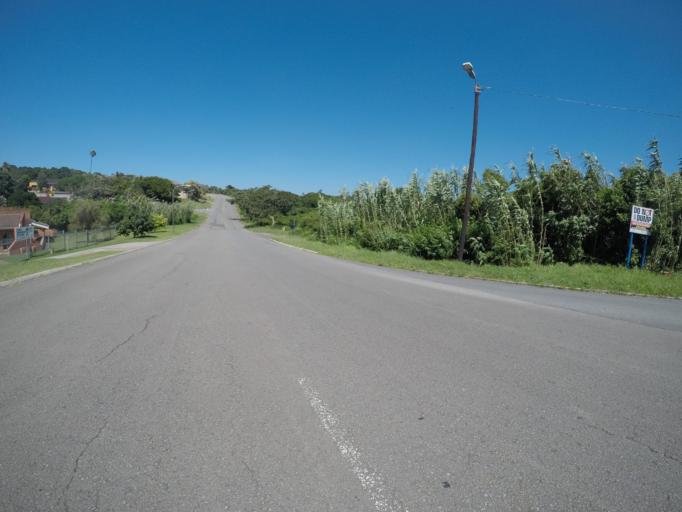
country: ZA
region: Eastern Cape
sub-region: Buffalo City Metropolitan Municipality
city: East London
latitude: -32.9731
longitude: 27.9471
